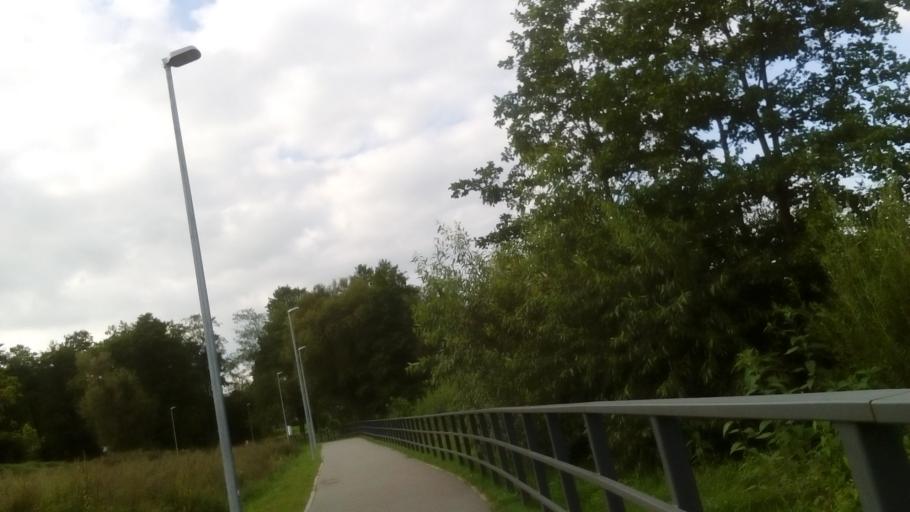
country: LT
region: Alytaus apskritis
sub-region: Alytus
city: Alytus
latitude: 54.4184
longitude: 24.0406
